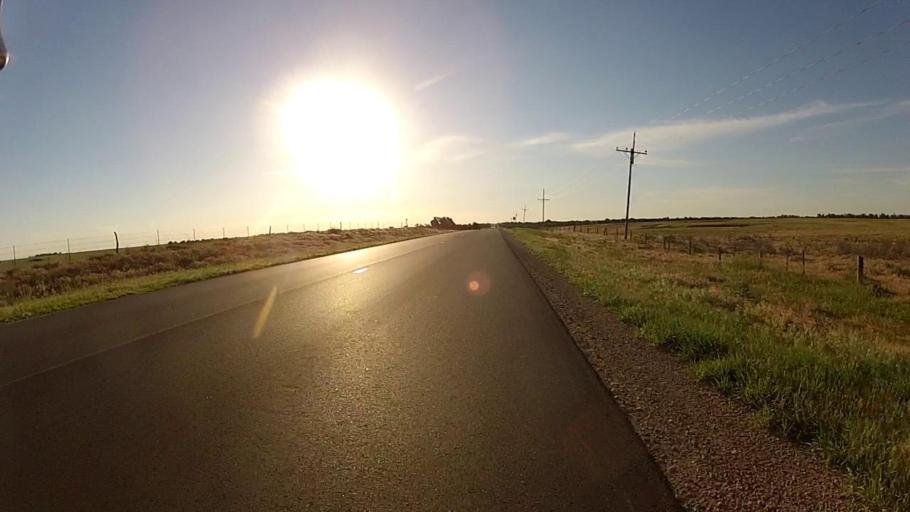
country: US
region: Kansas
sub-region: Comanche County
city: Coldwater
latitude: 37.2812
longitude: -99.2173
